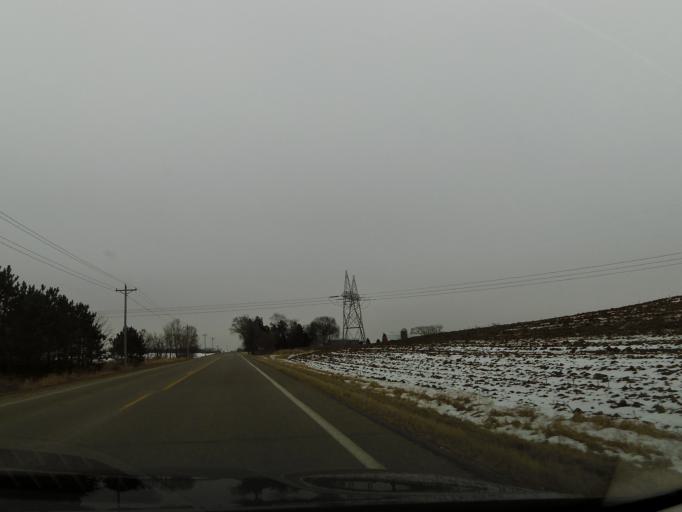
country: US
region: Minnesota
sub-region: Scott County
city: Jordan
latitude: 44.6306
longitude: -93.5803
